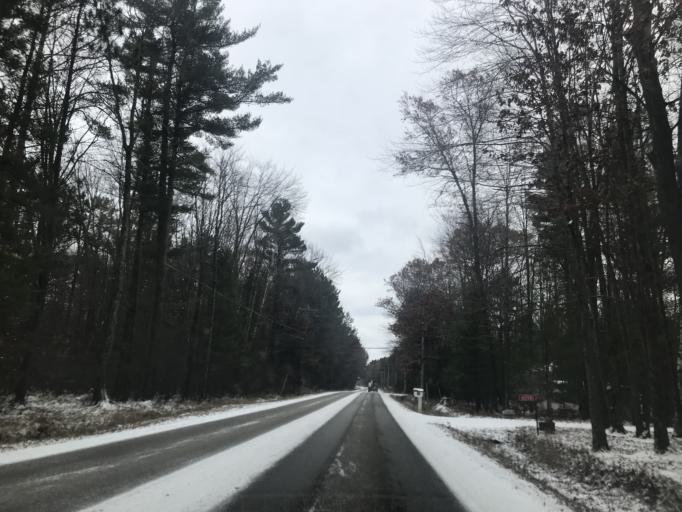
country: US
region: Wisconsin
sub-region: Marinette County
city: Marinette
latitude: 45.0675
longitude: -87.6594
